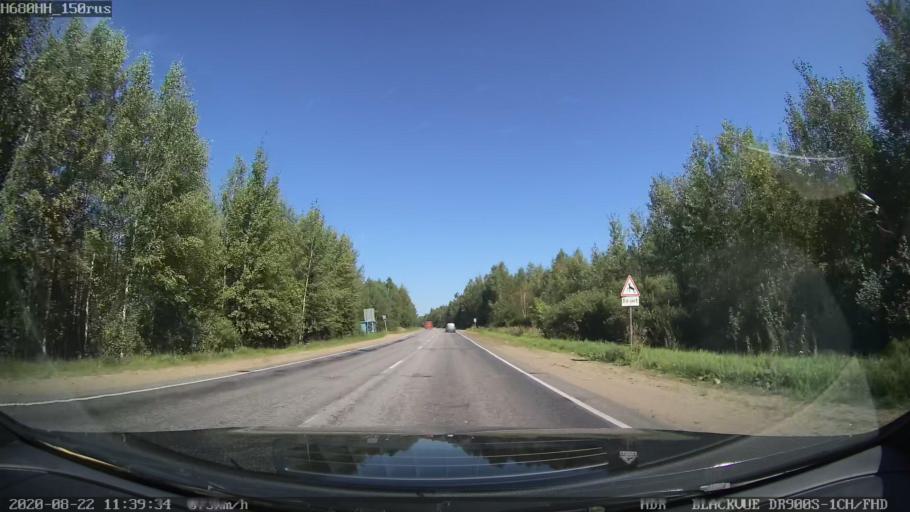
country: RU
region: Tverskaya
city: Sakharovo
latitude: 56.9664
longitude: 36.0222
